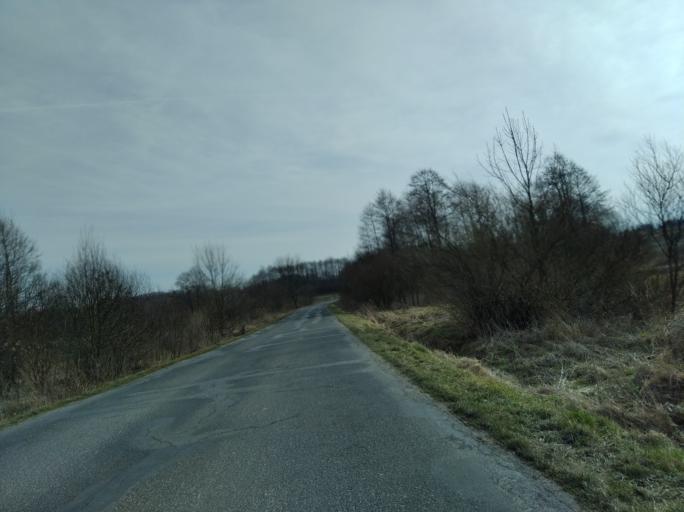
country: PL
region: Subcarpathian Voivodeship
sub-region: Powiat brzozowski
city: Stara Wies
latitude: 49.7159
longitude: 21.9808
